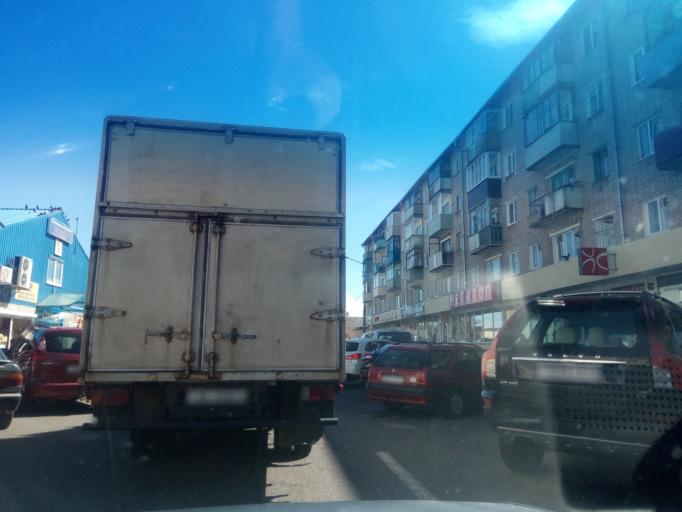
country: BY
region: Vitebsk
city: Polatsk
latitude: 55.4879
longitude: 28.7800
